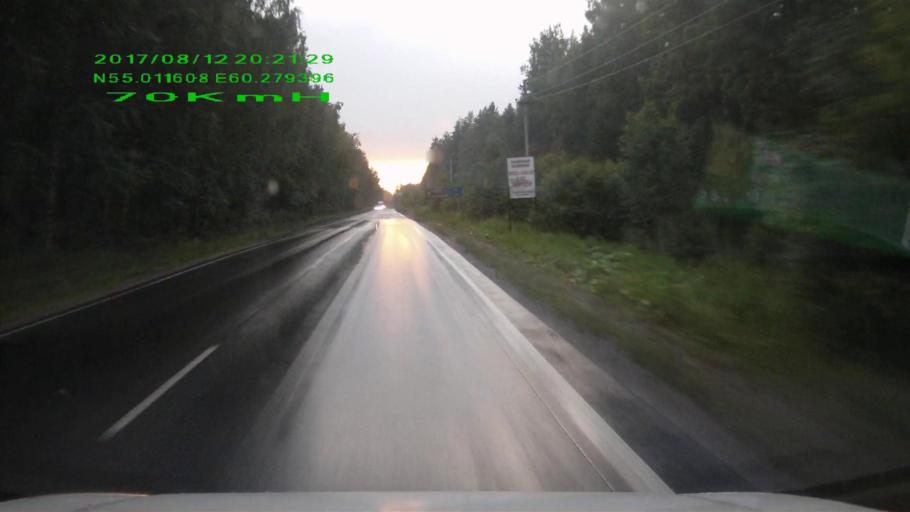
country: RU
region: Chelyabinsk
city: Chebarkul'
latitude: 55.0117
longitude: 60.2792
